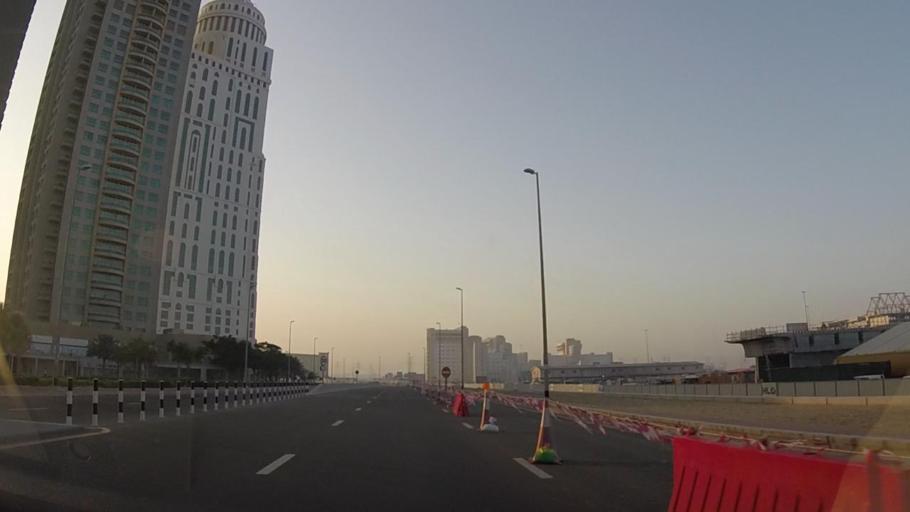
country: AE
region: Dubai
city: Dubai
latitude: 25.0644
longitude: 55.1368
